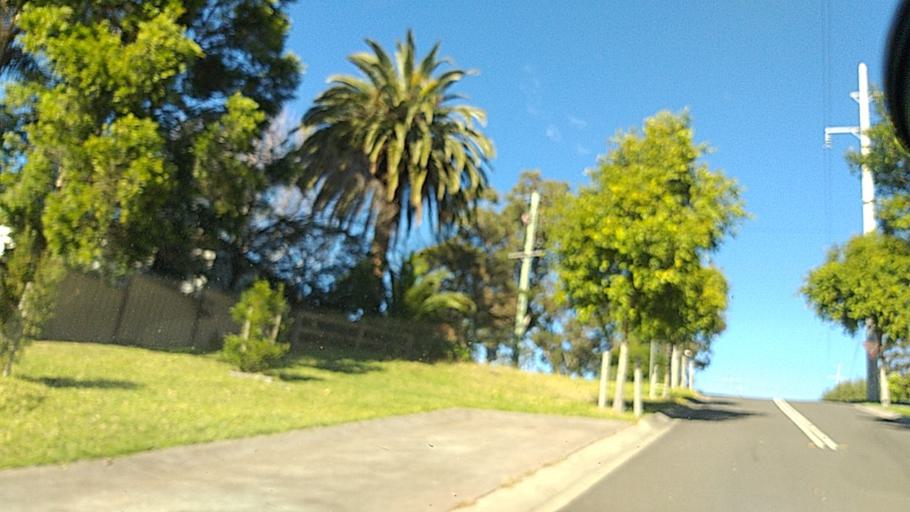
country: AU
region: New South Wales
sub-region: Wollongong
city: Mount Keira
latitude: -34.4299
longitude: 150.8497
